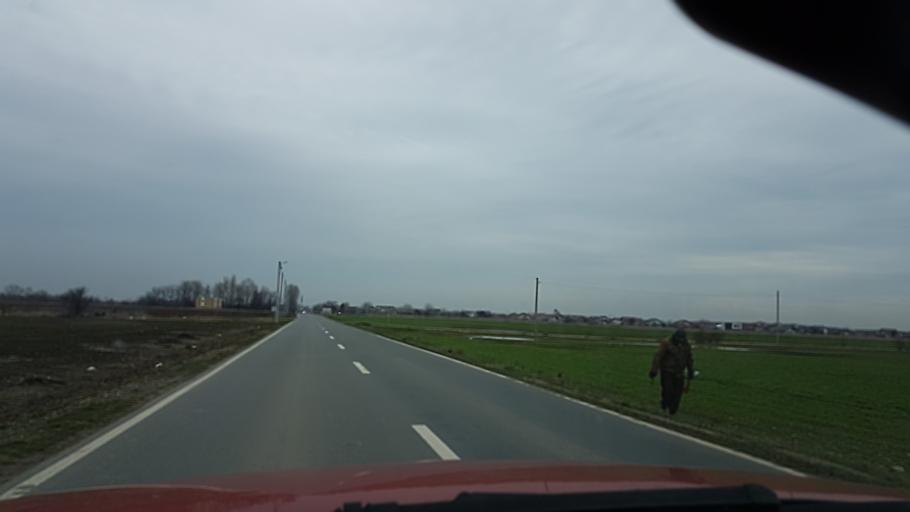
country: RO
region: Ilfov
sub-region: Comuna Tunari
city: Tunari
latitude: 44.5635
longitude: 26.1418
